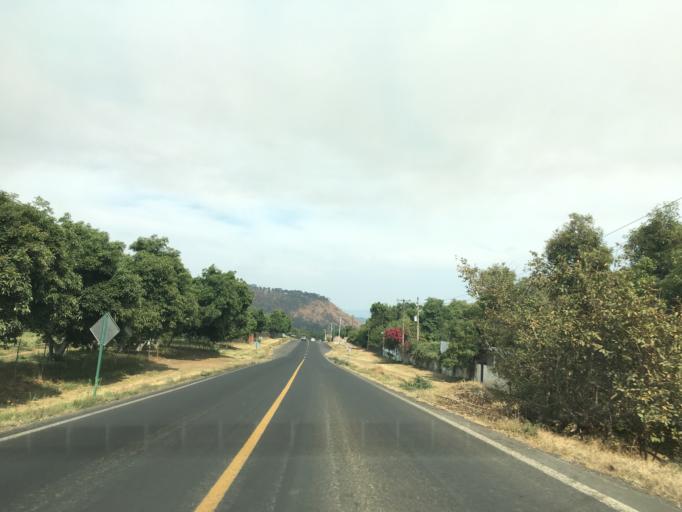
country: MX
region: Michoacan
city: Nuevo San Juan Parangaricutiro
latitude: 19.3935
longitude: -102.1048
